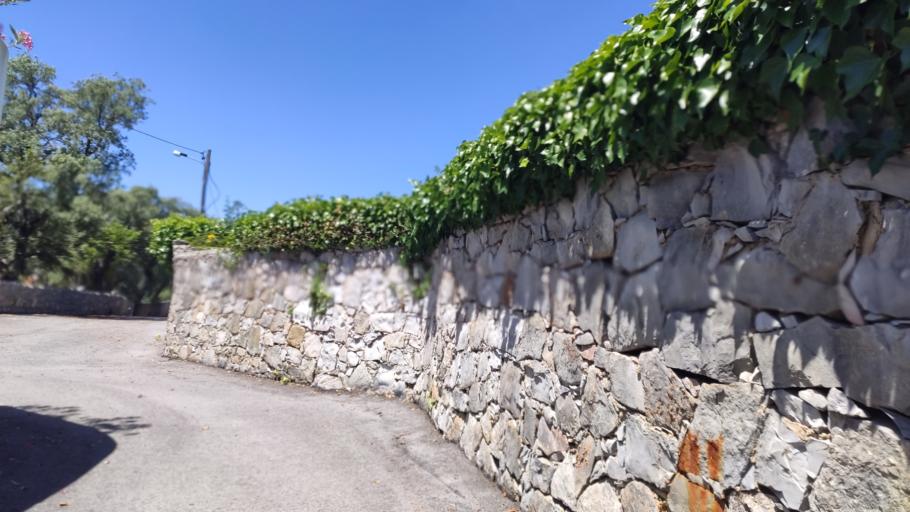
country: PT
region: Faro
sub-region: Sao Bras de Alportel
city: Sao Bras de Alportel
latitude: 37.1709
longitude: -7.9046
